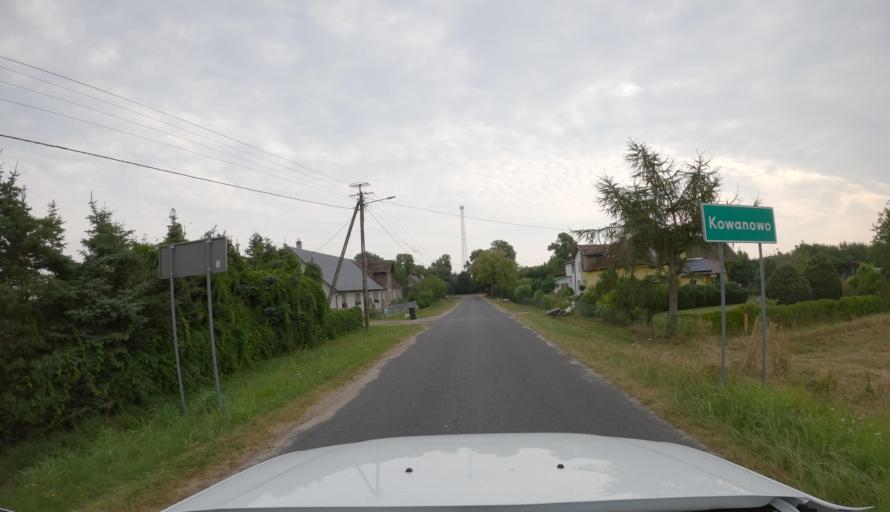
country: PL
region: West Pomeranian Voivodeship
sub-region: Powiat swidwinski
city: Slawoborze
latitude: 53.8054
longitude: 15.6066
